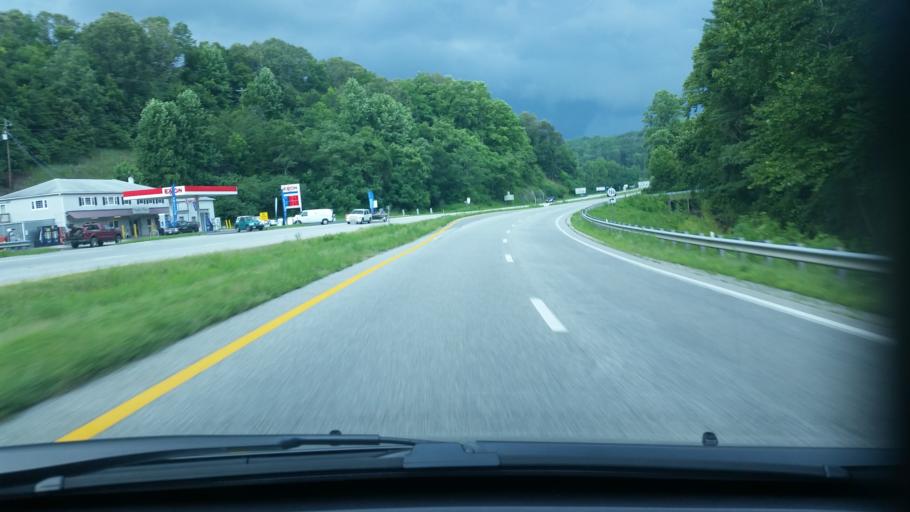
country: US
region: Virginia
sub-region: Nelson County
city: Nellysford
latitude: 37.8427
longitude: -78.8256
